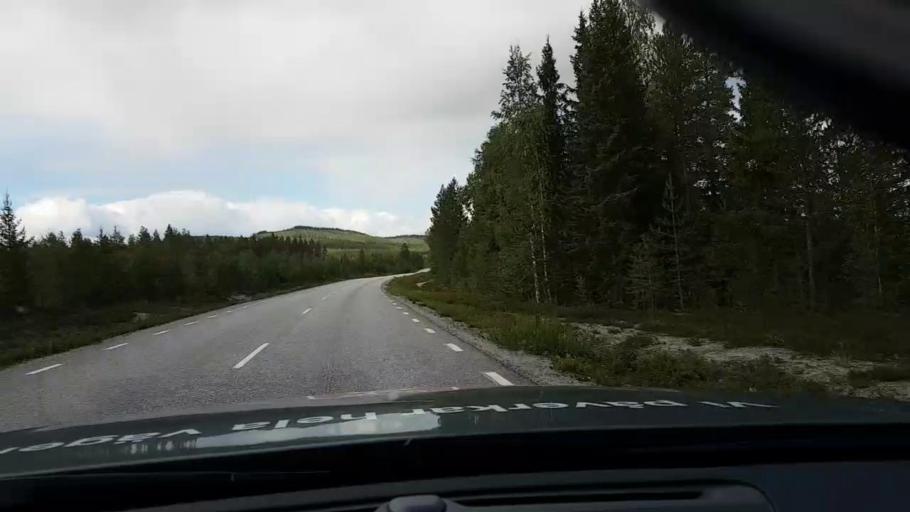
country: SE
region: Vaesternorrland
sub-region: OErnskoeldsviks Kommun
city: Bredbyn
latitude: 63.6797
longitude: 17.7871
